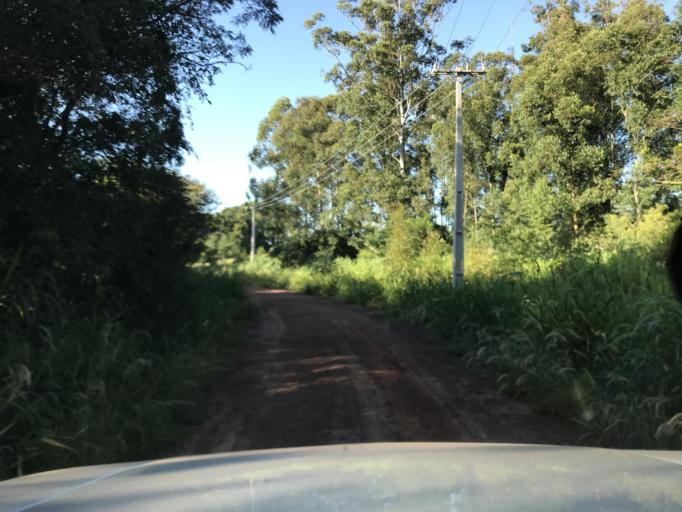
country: BR
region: Parana
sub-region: Palotina
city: Palotina
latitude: -24.2203
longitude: -53.7485
